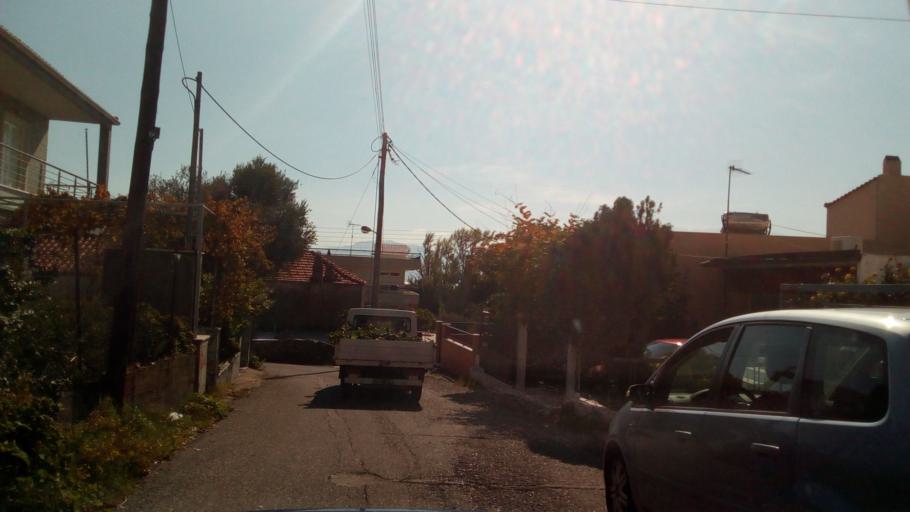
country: GR
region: West Greece
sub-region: Nomos Aitolias kai Akarnanias
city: Nafpaktos
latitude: 38.4151
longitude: 21.8746
